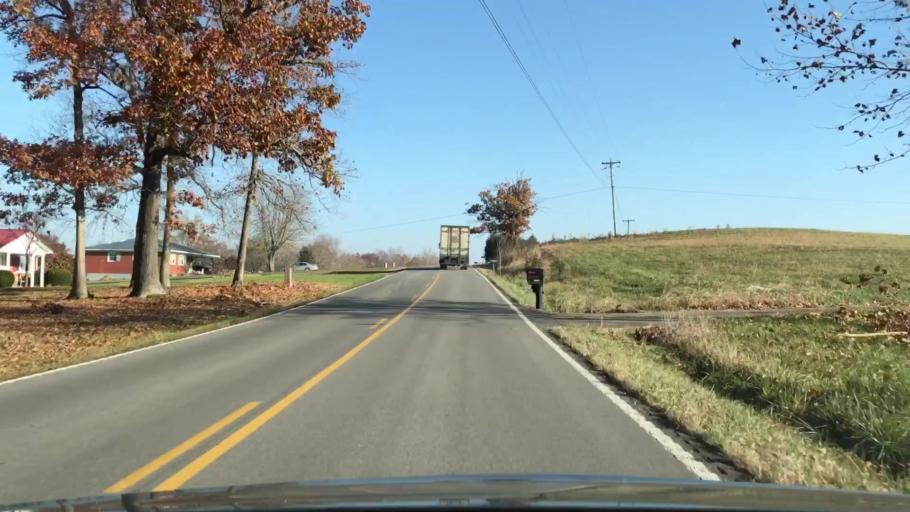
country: US
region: Kentucky
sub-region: Edmonson County
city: Brownsville
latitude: 37.3217
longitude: -86.2683
